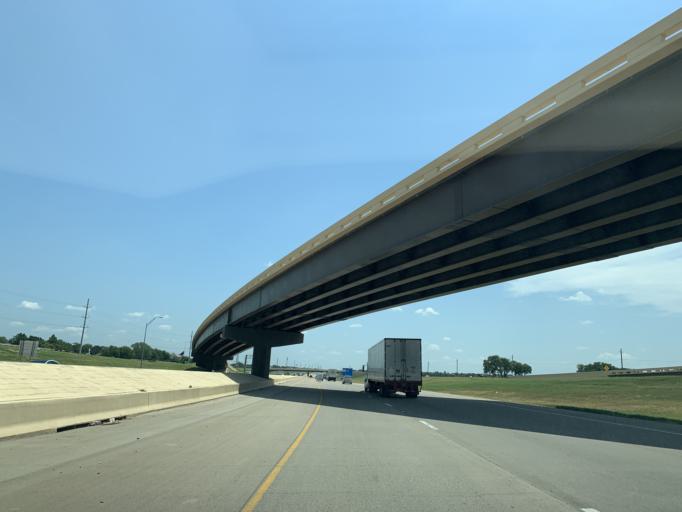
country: US
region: Texas
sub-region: Denton County
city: Roanoke
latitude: 32.9989
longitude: -97.2135
